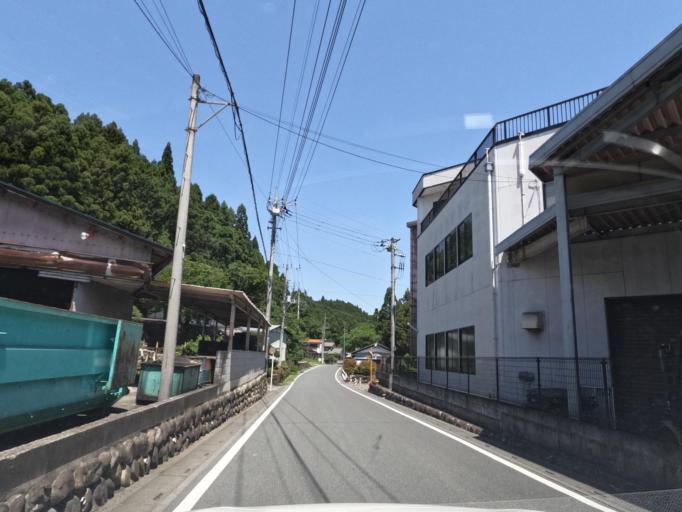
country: JP
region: Saitama
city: Chichibu
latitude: 36.0146
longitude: 139.1084
